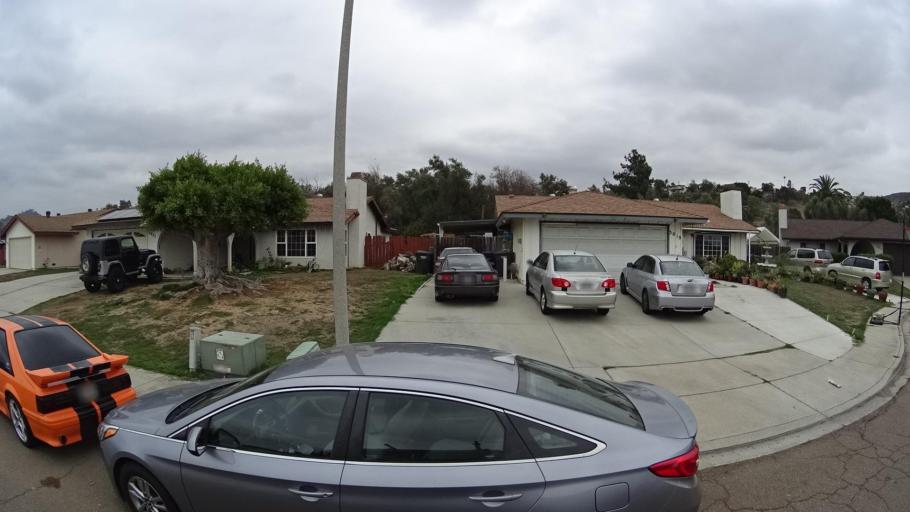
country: US
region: California
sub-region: San Diego County
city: Spring Valley
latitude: 32.7377
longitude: -117.0020
